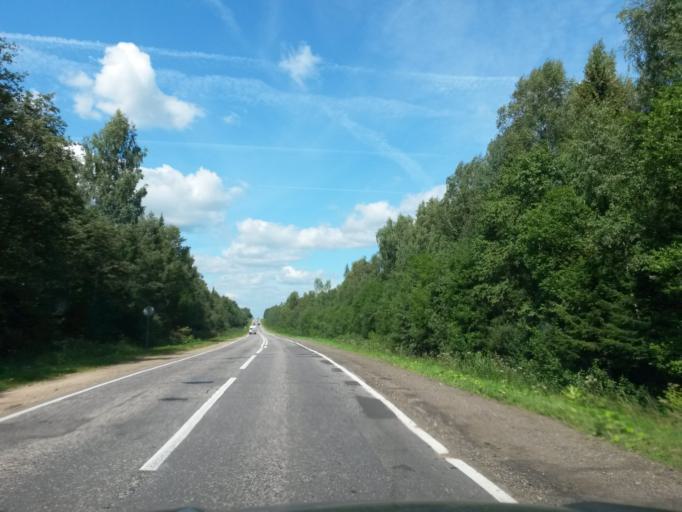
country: RU
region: Jaroslavl
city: Krasnyye Tkachi
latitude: 57.4731
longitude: 39.9082
